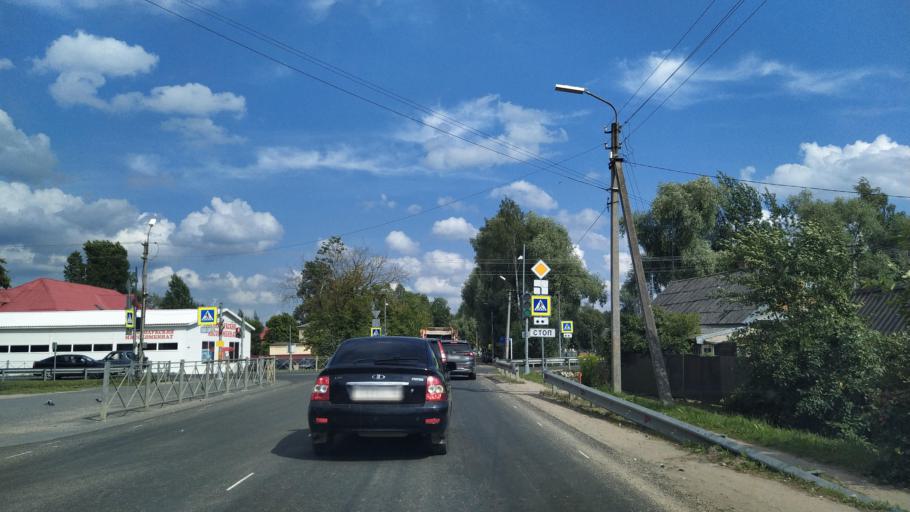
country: RU
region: Pskov
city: Porkhov
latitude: 57.7610
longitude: 29.5560
